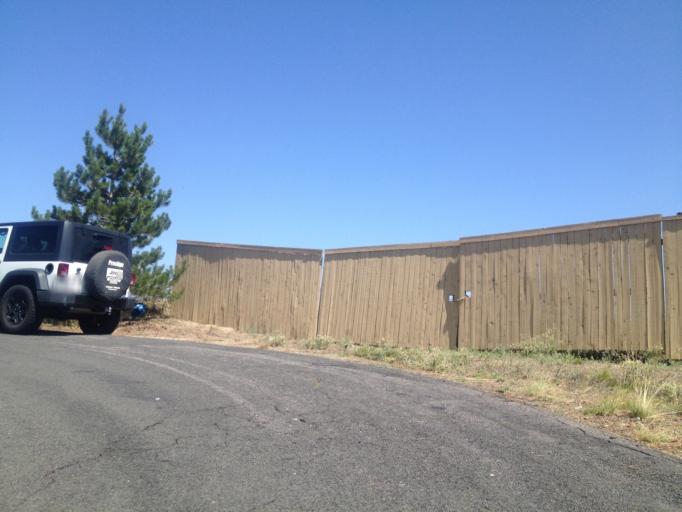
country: US
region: Colorado
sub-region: Boulder County
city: Louisville
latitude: 39.9602
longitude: -105.1424
